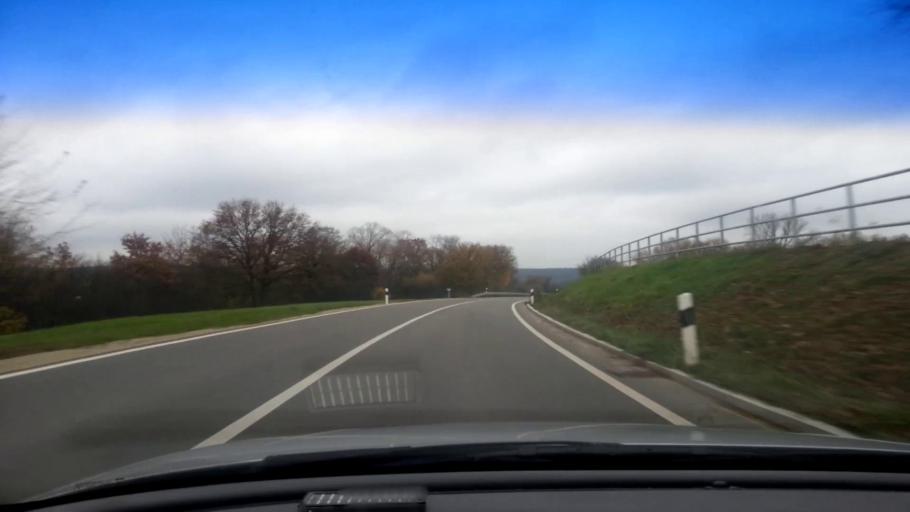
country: DE
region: Bavaria
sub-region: Upper Franconia
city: Pettstadt
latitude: 49.8416
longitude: 10.9316
